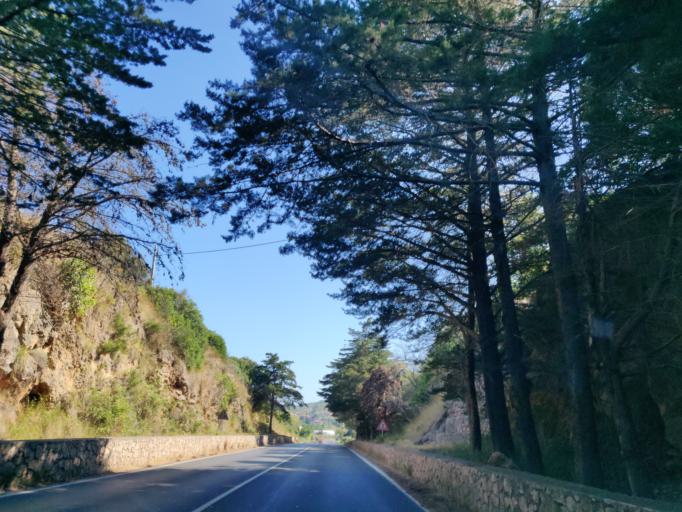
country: IT
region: Tuscany
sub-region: Provincia di Grosseto
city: Porto Ercole
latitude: 42.4075
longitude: 11.2003
